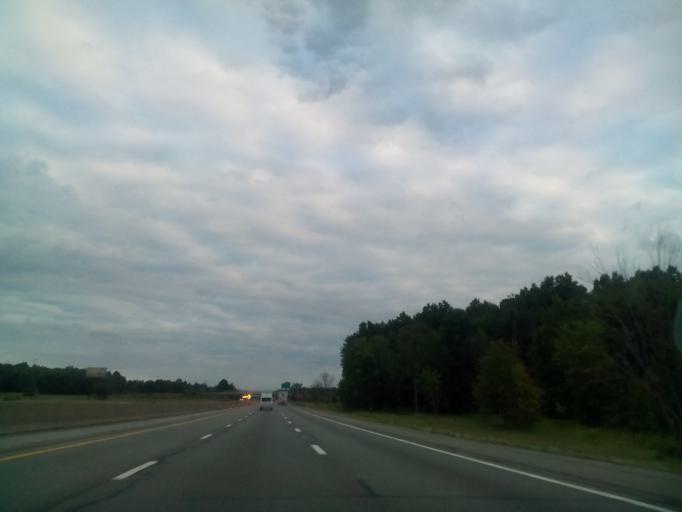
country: US
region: Ohio
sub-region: Trumbull County
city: Lordstown
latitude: 41.1615
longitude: -80.9043
